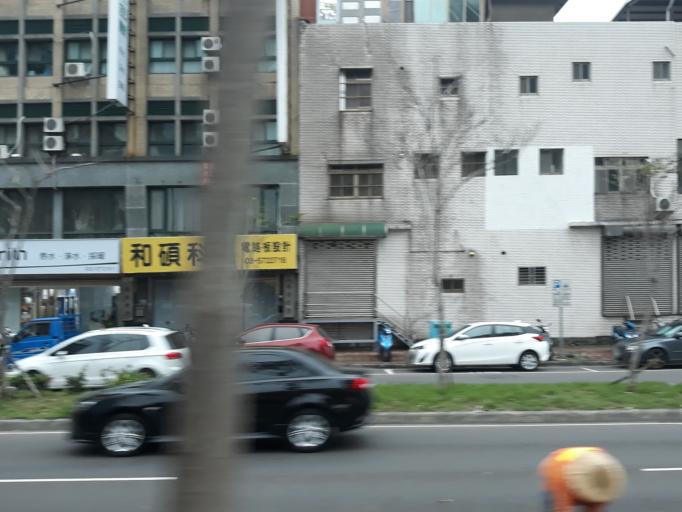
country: TW
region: Taiwan
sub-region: Hsinchu
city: Hsinchu
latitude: 24.7993
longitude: 121.0050
